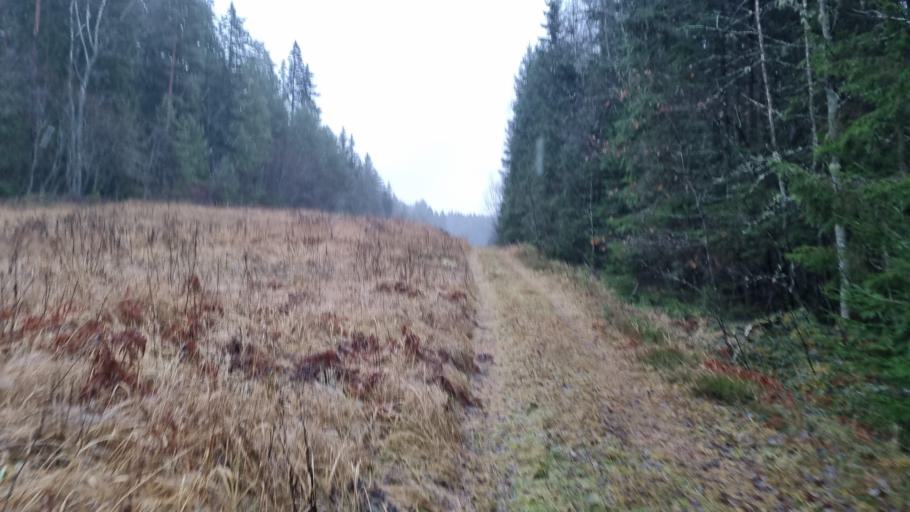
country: LV
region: Ligatne
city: Ligatne
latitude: 57.2418
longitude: 25.1556
